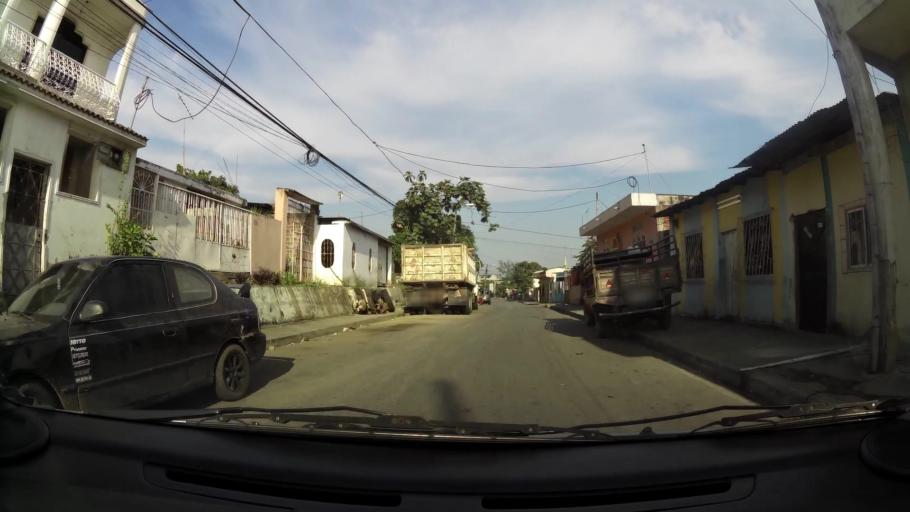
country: EC
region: Guayas
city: Eloy Alfaro
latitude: -2.0727
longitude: -79.9295
